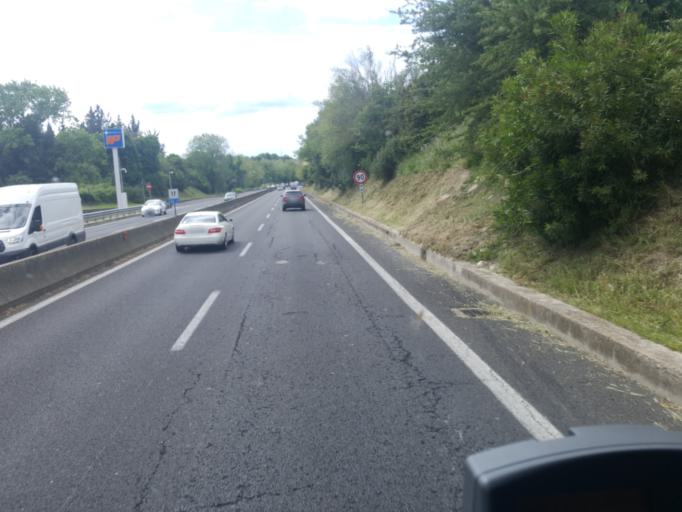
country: IT
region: Latium
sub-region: Citta metropolitana di Roma Capitale
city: La Massimina-Casal Lumbroso
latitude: 41.8877
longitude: 12.3084
